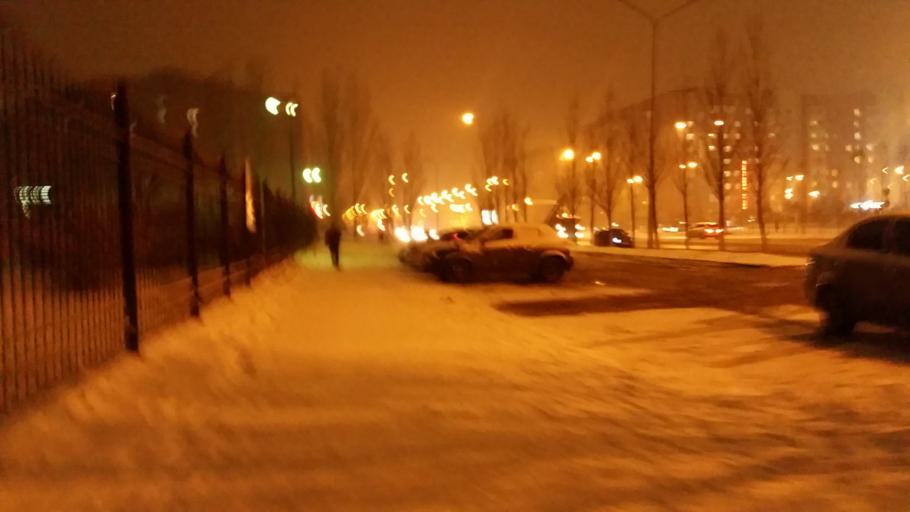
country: KZ
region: Astana Qalasy
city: Astana
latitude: 51.1506
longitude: 71.4822
